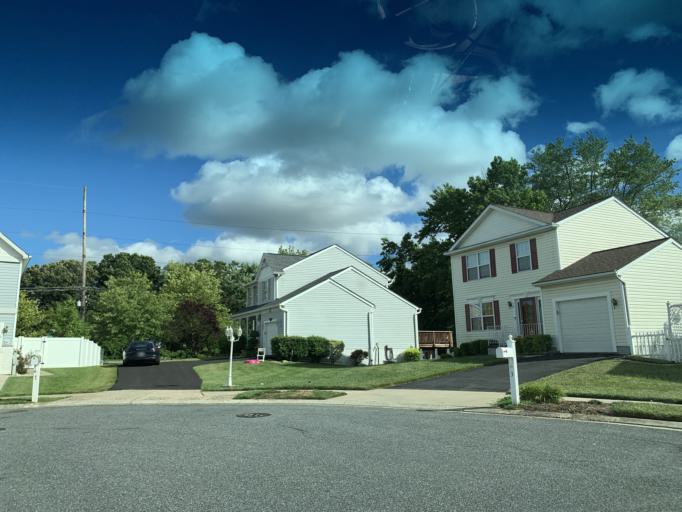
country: US
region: Maryland
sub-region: Baltimore County
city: Middle River
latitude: 39.3540
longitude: -76.4362
